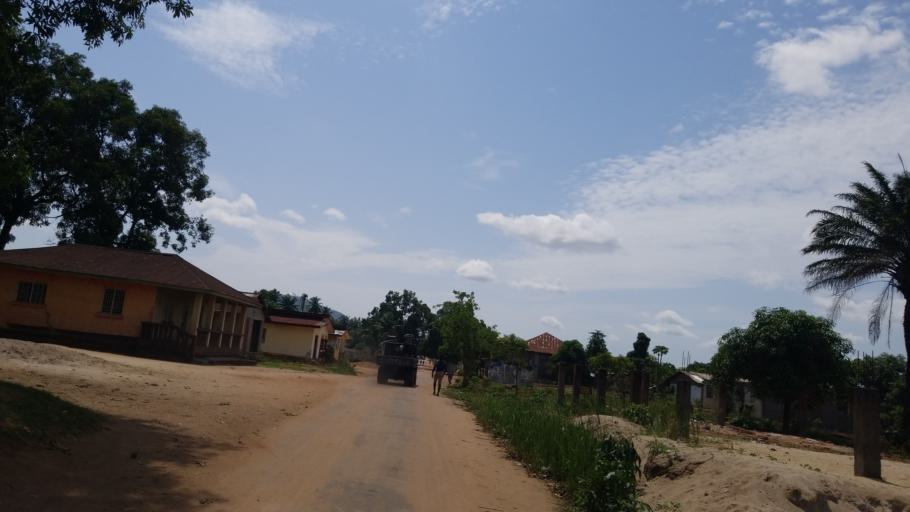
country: SL
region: Western Area
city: Waterloo
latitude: 8.3086
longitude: -13.0520
